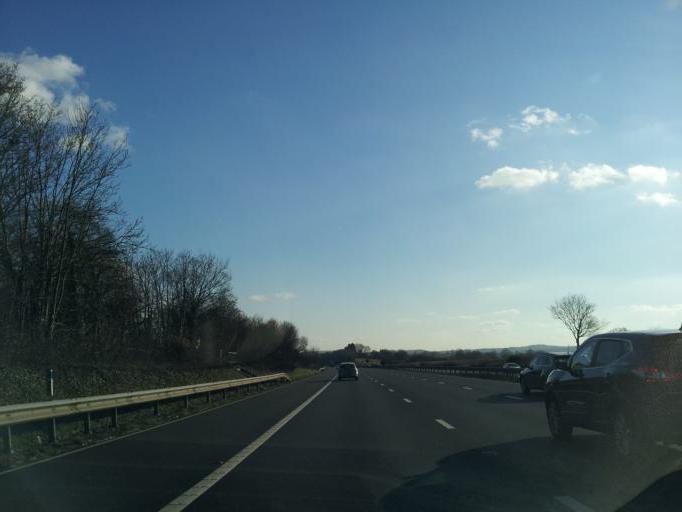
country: GB
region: England
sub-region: Devon
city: Cullompton
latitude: 50.8894
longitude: -3.3776
